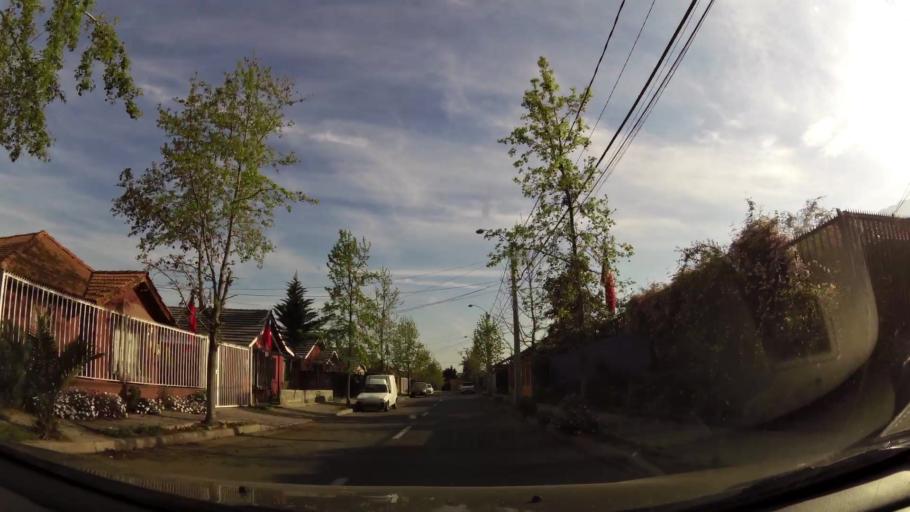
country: CL
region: Santiago Metropolitan
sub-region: Provincia de Cordillera
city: Puente Alto
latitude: -33.5695
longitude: -70.5456
